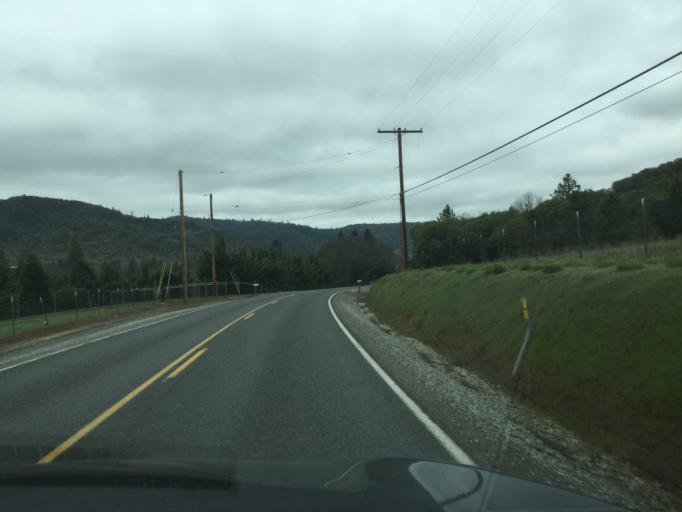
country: US
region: Oregon
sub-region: Jackson County
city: Gold Hill
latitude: 42.3986
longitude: -123.0185
